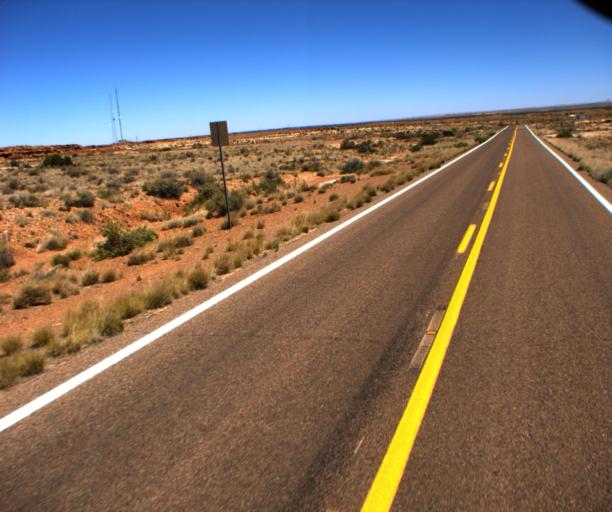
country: US
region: Arizona
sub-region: Navajo County
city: Winslow
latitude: 34.9635
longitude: -110.6470
